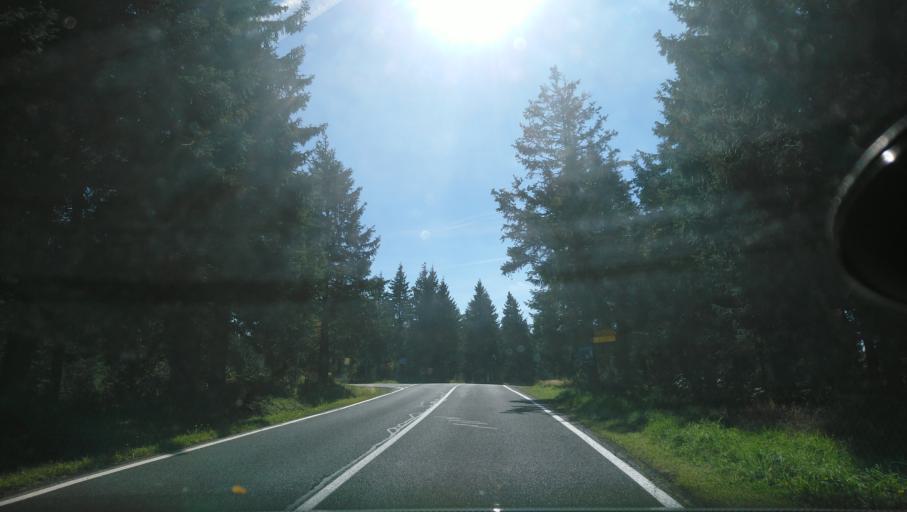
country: DE
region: Saxony
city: Kurort Oberwiesenthal
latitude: 50.4027
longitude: 12.9511
